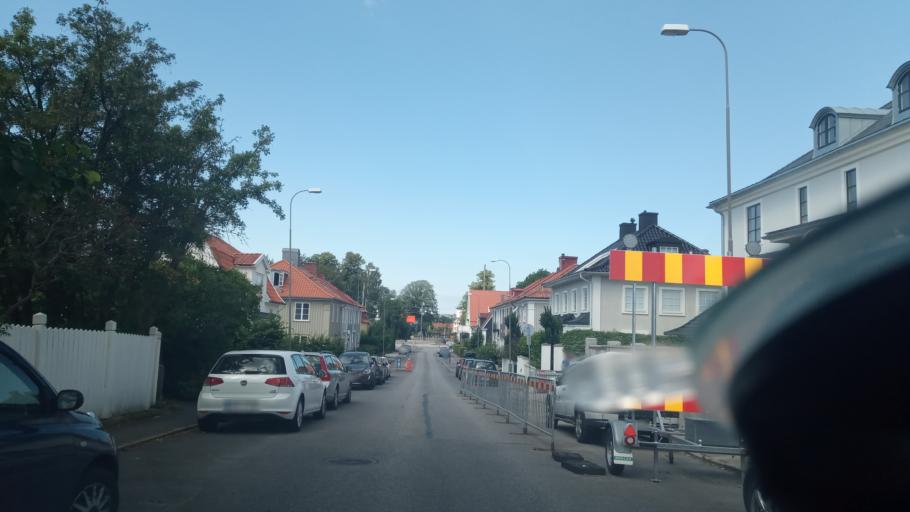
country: SE
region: Vaestra Goetaland
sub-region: Goteborg
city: Goeteborg
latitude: 57.6969
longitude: 12.0016
